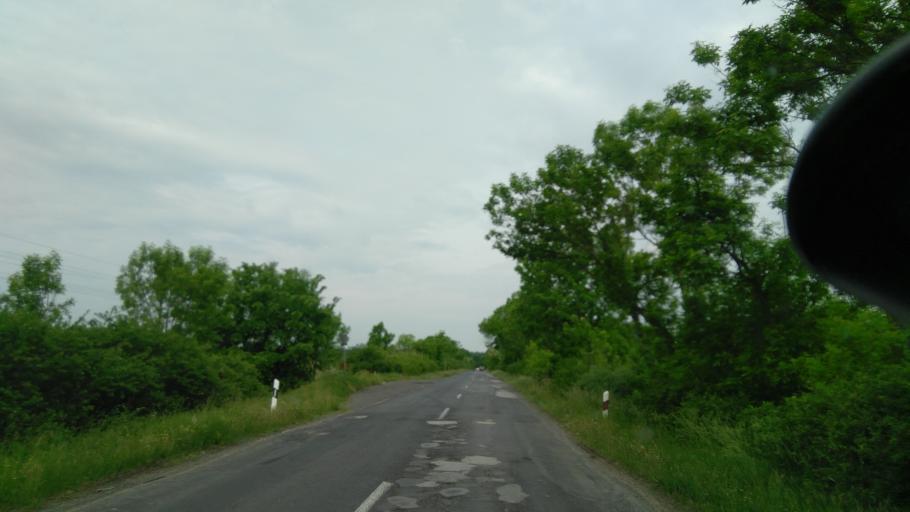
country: HU
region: Bekes
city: Szeghalom
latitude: 46.9740
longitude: 21.1984
